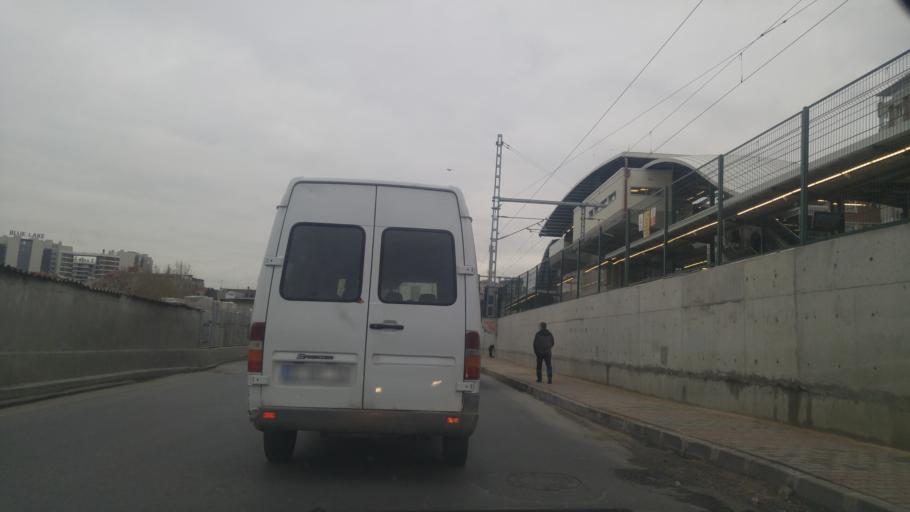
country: TR
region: Istanbul
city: Mahmutbey
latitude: 40.9879
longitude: 28.7729
